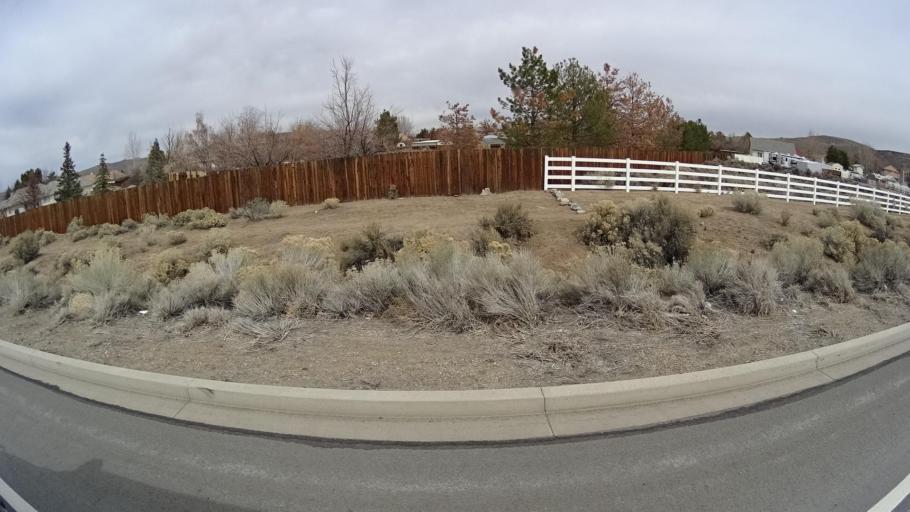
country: US
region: Nevada
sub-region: Washoe County
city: Spanish Springs
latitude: 39.6362
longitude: -119.6837
